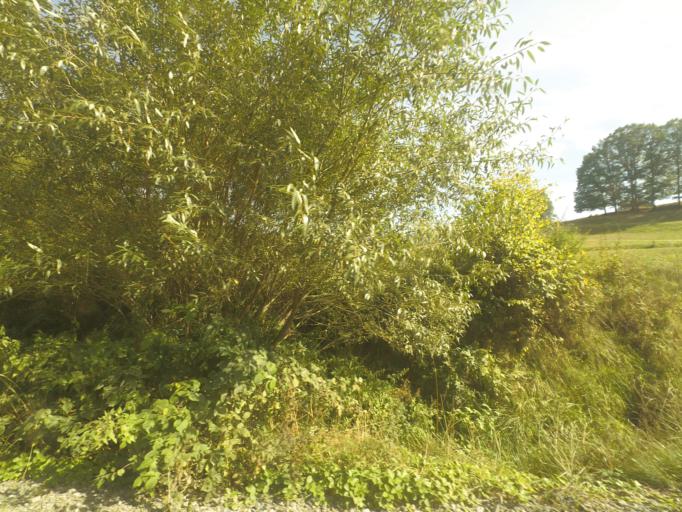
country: DE
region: Thuringia
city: Metzels
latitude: 50.6549
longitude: 10.4395
